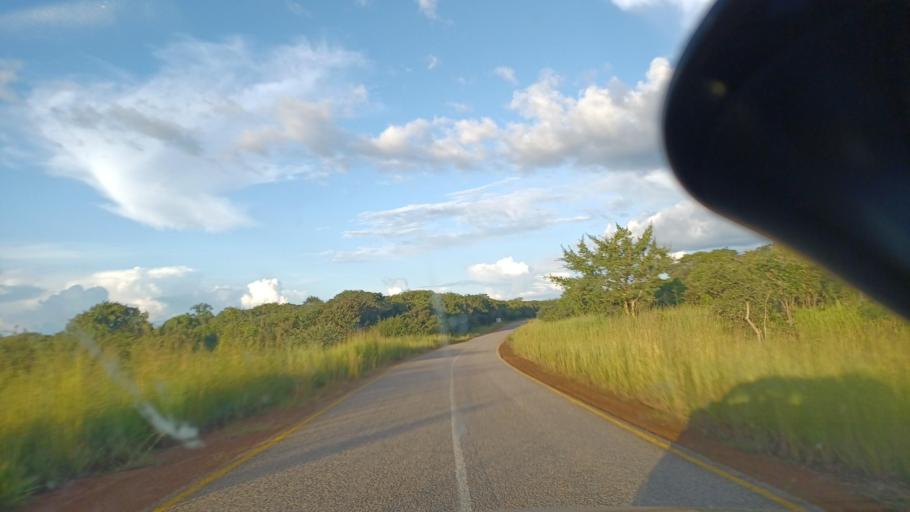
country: ZM
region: North-Western
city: Kalengwa
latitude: -13.0905
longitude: 25.2507
